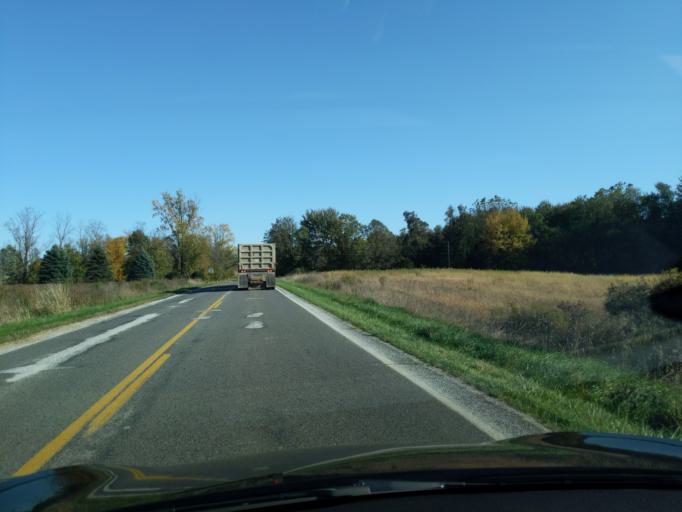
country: US
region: Michigan
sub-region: Clinton County
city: Saint Johns
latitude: 42.9303
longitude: -84.4926
